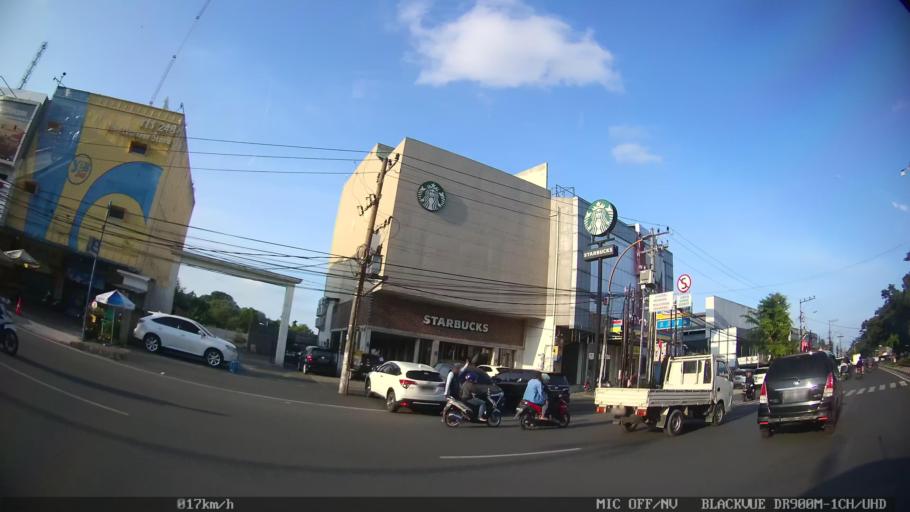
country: ID
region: North Sumatra
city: Medan
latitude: 3.6068
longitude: 98.6693
